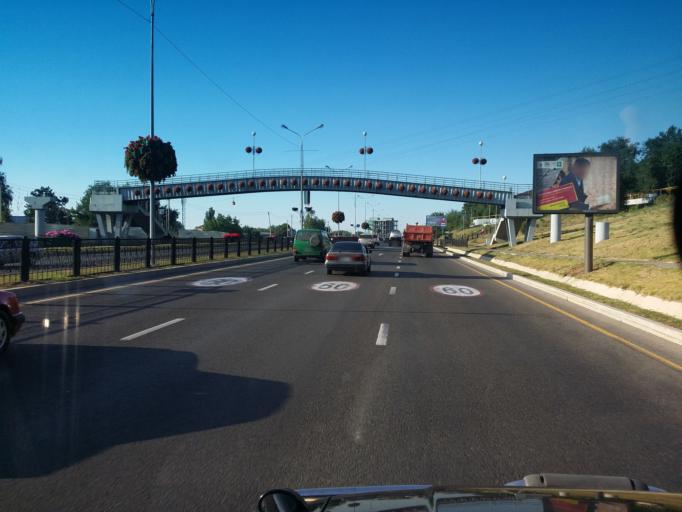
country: KZ
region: Almaty Qalasy
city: Almaty
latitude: 43.2336
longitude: 76.9694
